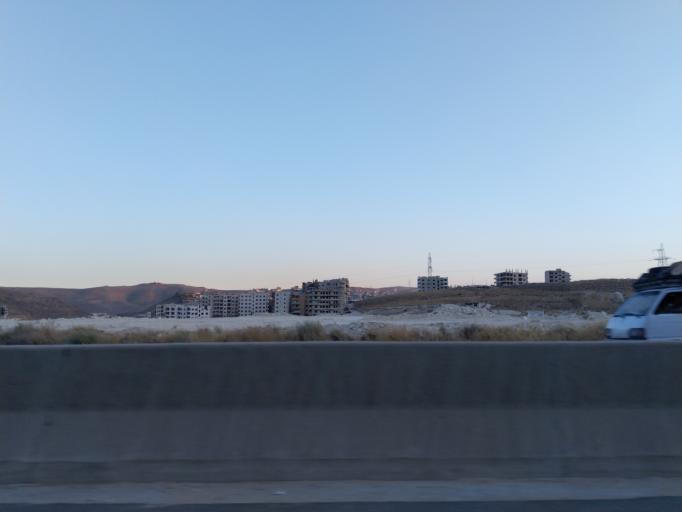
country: SY
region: Rif-dimashq
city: At Tall
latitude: 33.5859
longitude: 36.2992
